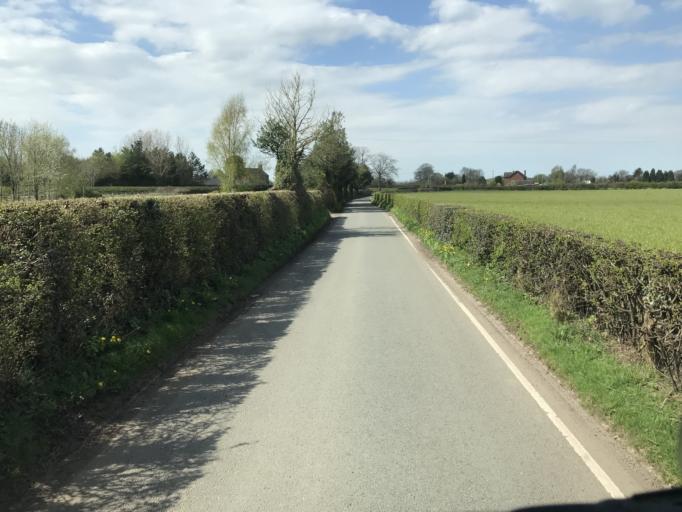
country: GB
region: England
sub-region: Cheshire West and Chester
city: Tarvin
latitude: 53.2041
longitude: -2.7613
